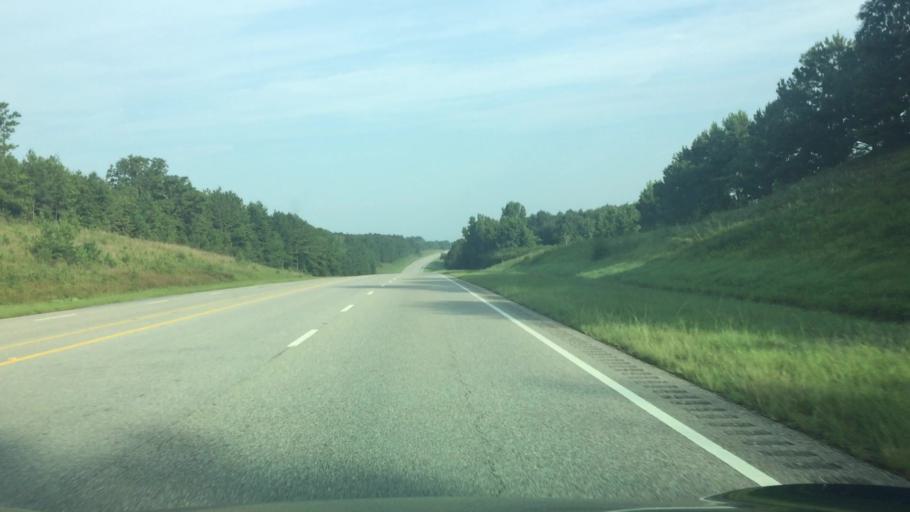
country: US
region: Alabama
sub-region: Covington County
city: Andalusia
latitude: 31.4467
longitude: -86.6192
